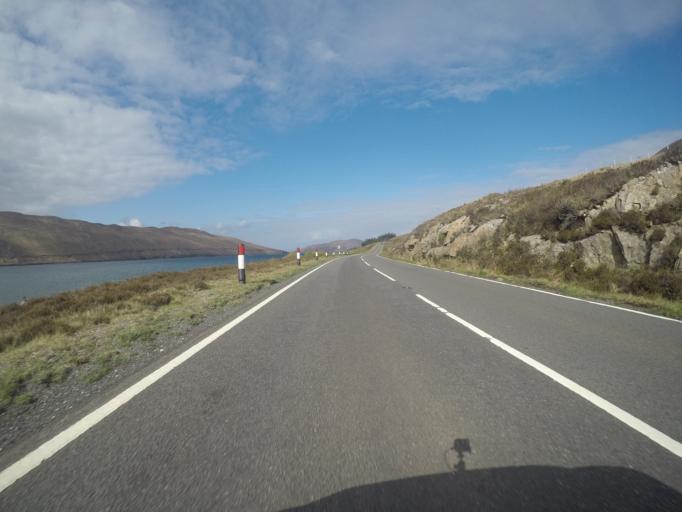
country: GB
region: Scotland
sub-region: Highland
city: Portree
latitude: 57.2706
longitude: -6.0646
